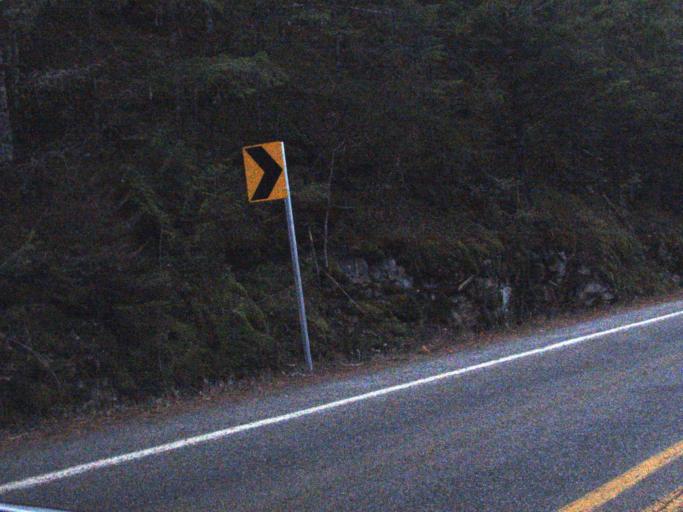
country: US
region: Washington
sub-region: Snohomish County
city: Darrington
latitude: 48.7107
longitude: -121.1472
